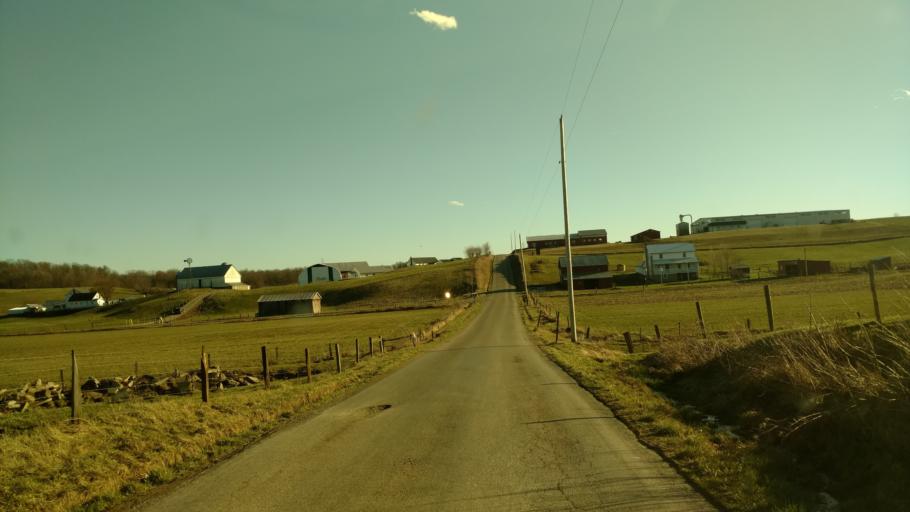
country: US
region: Ohio
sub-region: Wayne County
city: Apple Creek
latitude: 40.6136
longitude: -81.7609
